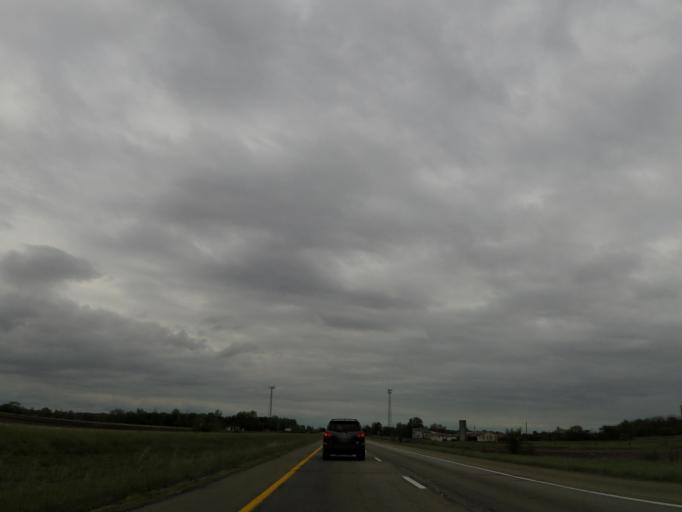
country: US
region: Ohio
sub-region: Madison County
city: Mount Sterling
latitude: 39.7786
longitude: -83.2615
